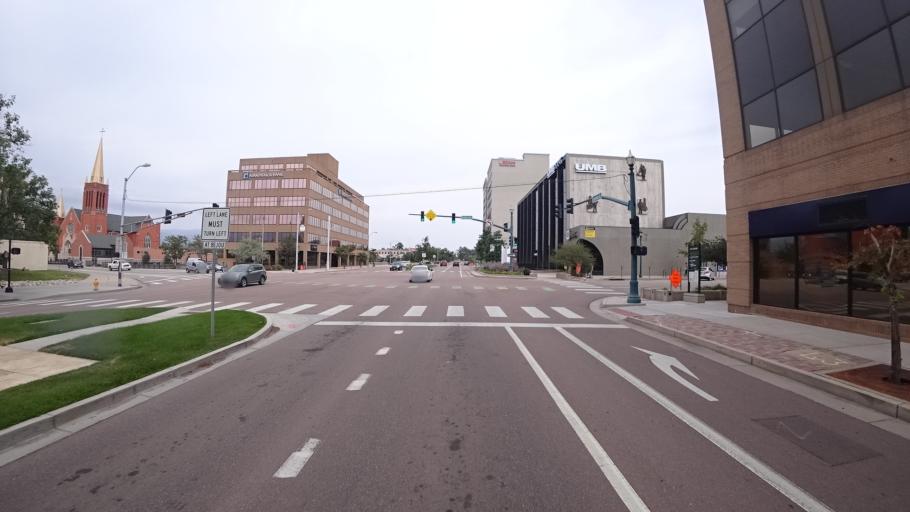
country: US
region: Colorado
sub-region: El Paso County
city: Colorado Springs
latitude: 38.8352
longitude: -104.8252
